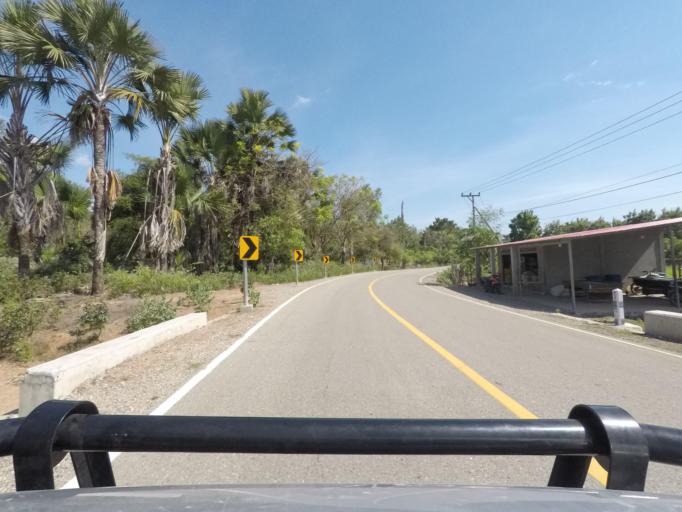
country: TL
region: Bobonaro
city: Maliana
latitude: -8.8788
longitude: 125.0371
